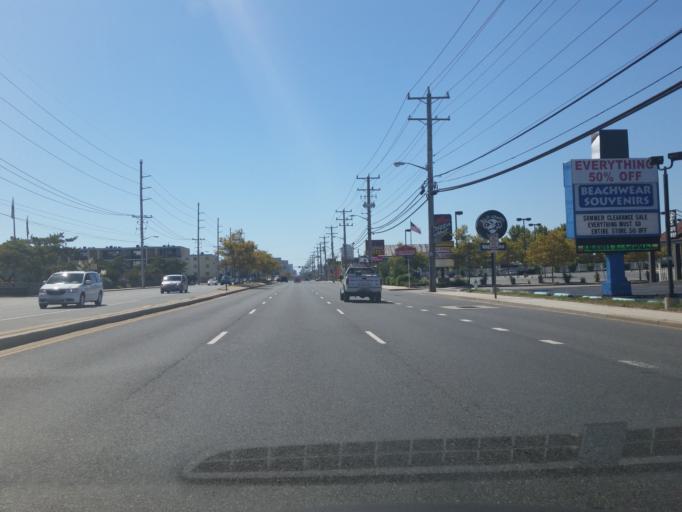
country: US
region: Delaware
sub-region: Sussex County
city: Bethany Beach
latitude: 38.4381
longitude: -75.0540
